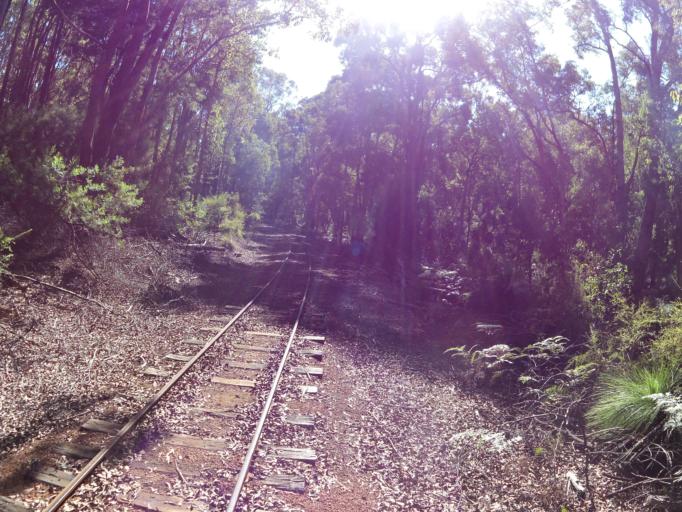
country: AU
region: Western Australia
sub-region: Waroona
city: Waroona
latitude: -32.7161
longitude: 116.0965
